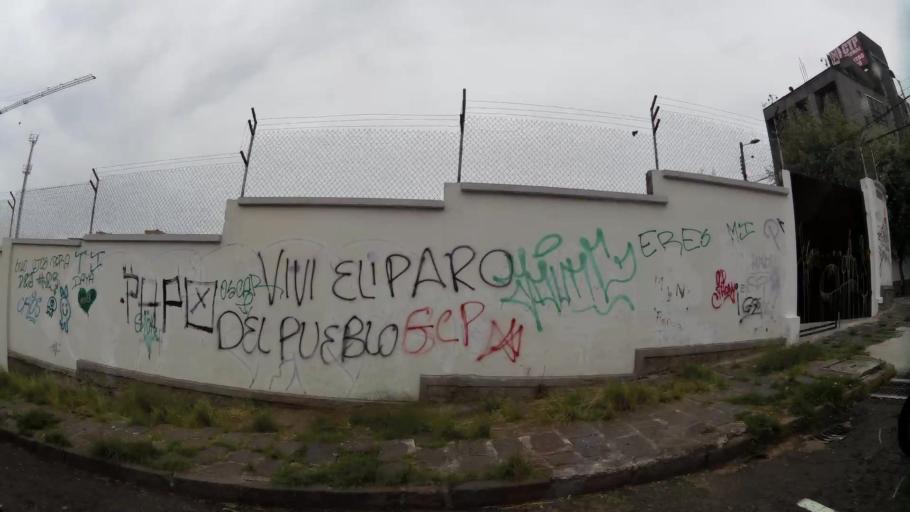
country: EC
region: Pichincha
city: Quito
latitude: -0.2077
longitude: -78.5030
